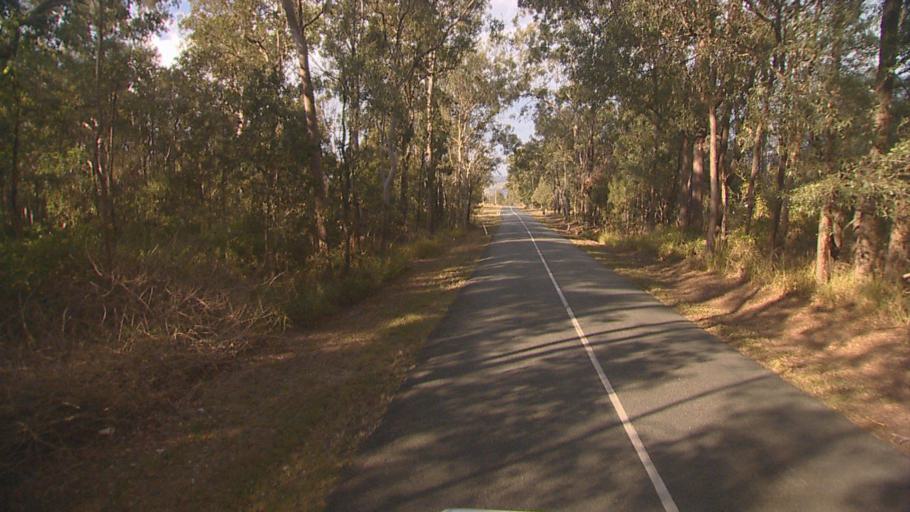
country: AU
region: Queensland
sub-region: Gold Coast
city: Ormeau Hills
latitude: -27.8456
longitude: 153.1480
